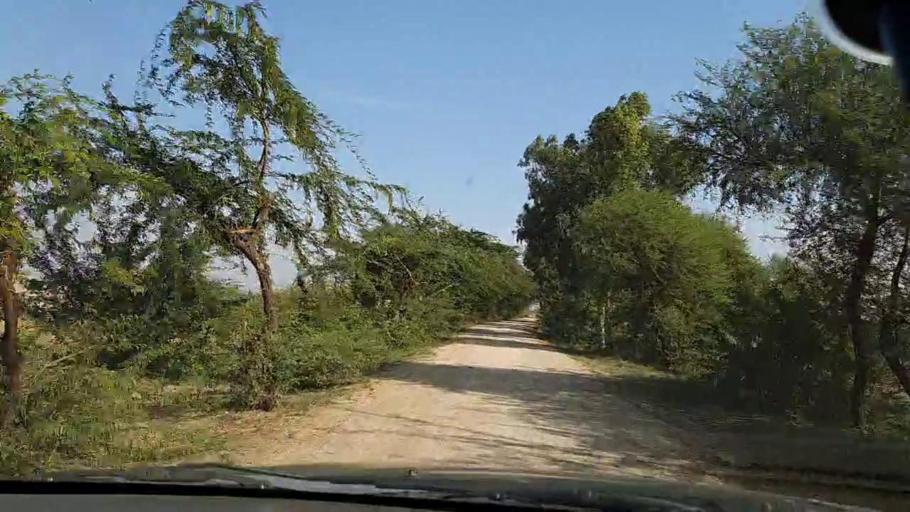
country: PK
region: Sindh
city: Mirpur Batoro
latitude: 24.6290
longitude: 68.2679
